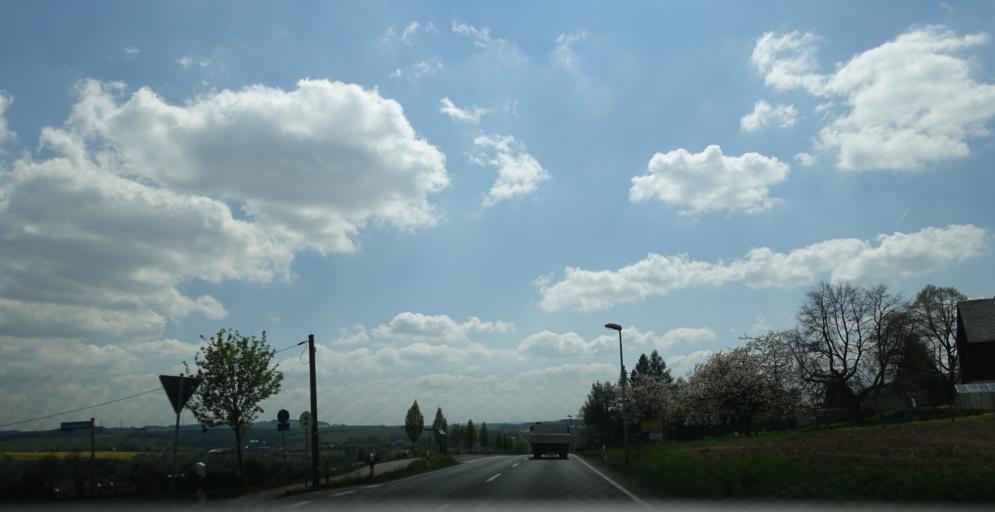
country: DE
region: Saxony
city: Grosshartmannsdorf
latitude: 50.8145
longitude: 13.3242
